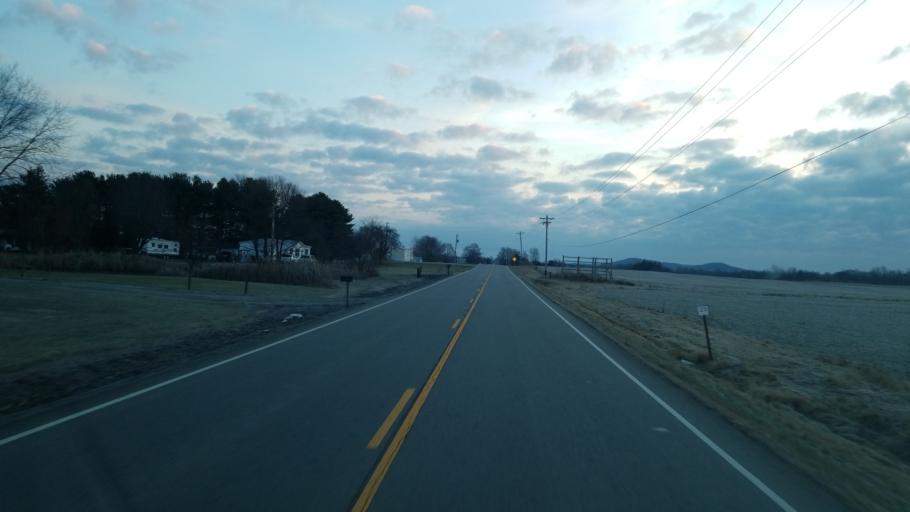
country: US
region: Ohio
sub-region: Highland County
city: Greenfield
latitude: 39.2168
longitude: -83.4467
